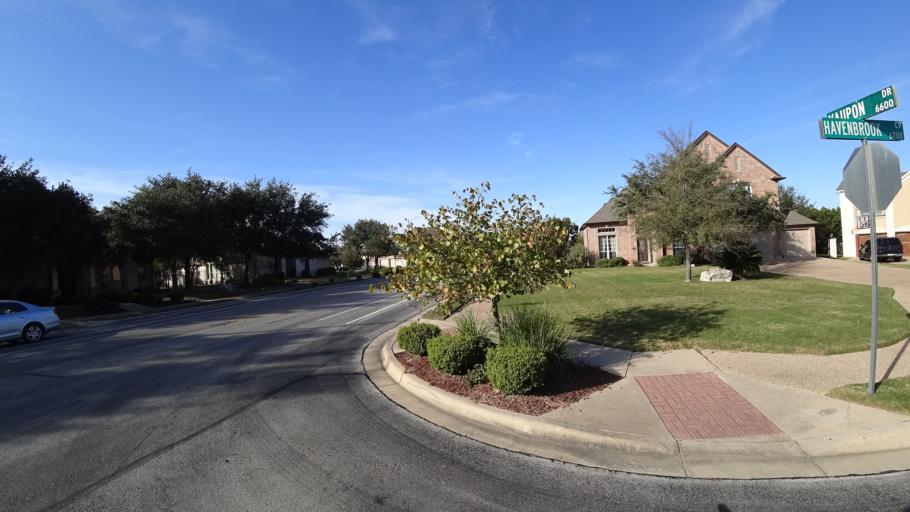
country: US
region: Texas
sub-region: Williamson County
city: Jollyville
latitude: 30.4021
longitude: -97.7763
